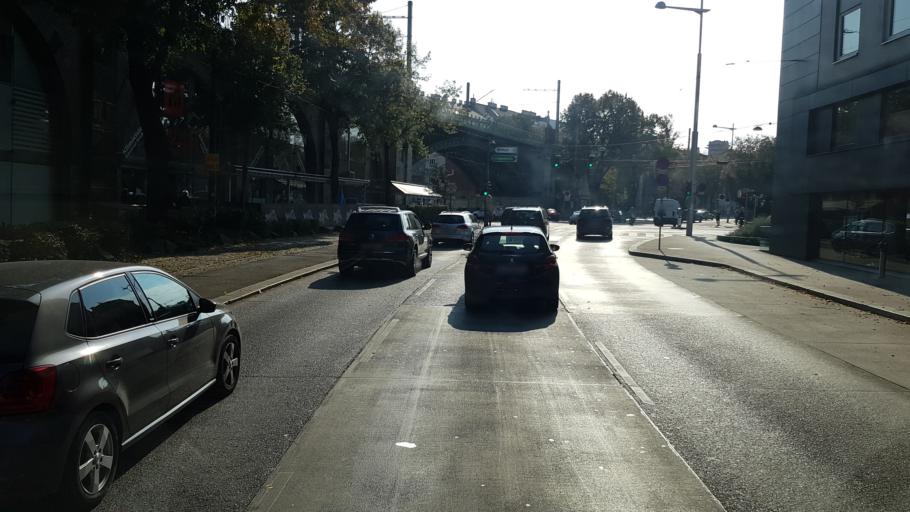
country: AT
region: Vienna
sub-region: Wien Stadt
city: Vienna
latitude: 48.2328
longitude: 16.3543
